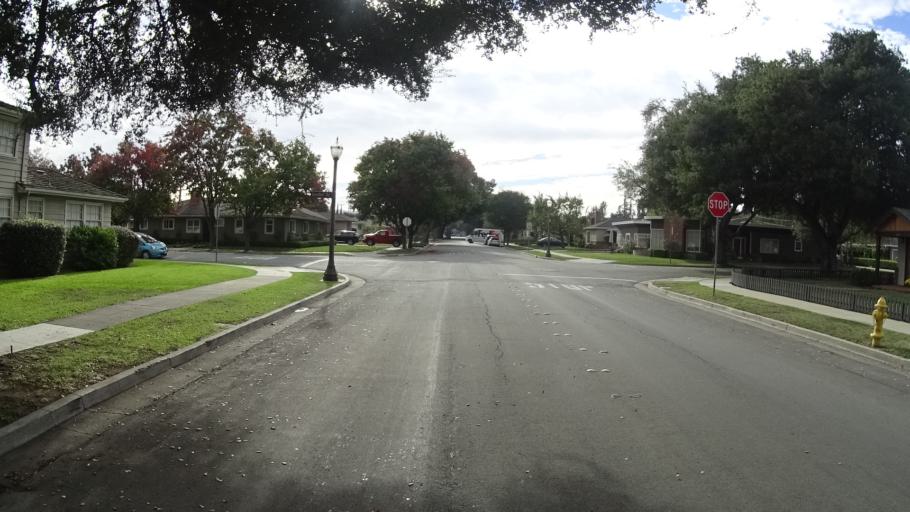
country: US
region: California
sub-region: Santa Clara County
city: Burbank
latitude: 37.3344
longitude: -121.9330
